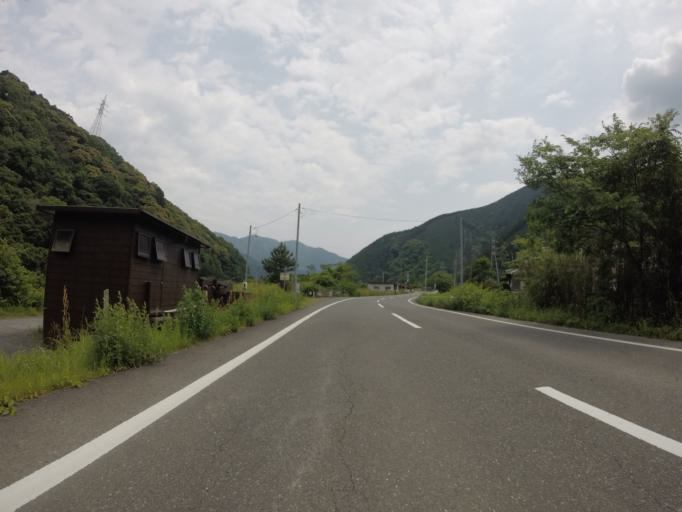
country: JP
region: Shizuoka
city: Shizuoka-shi
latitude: 35.1152
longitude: 138.3514
